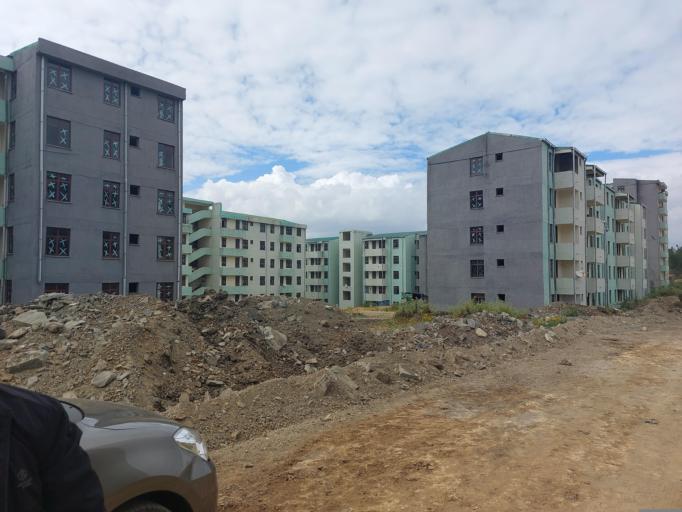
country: ET
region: Adis Abeba
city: Addis Ababa
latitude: 8.9628
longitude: 38.8821
